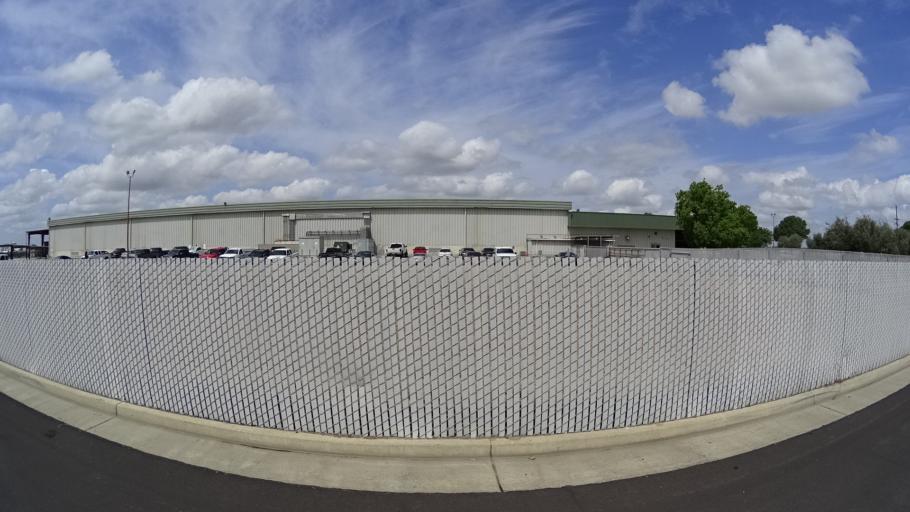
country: US
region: California
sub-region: Kings County
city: Home Garden
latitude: 36.2830
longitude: -119.6505
